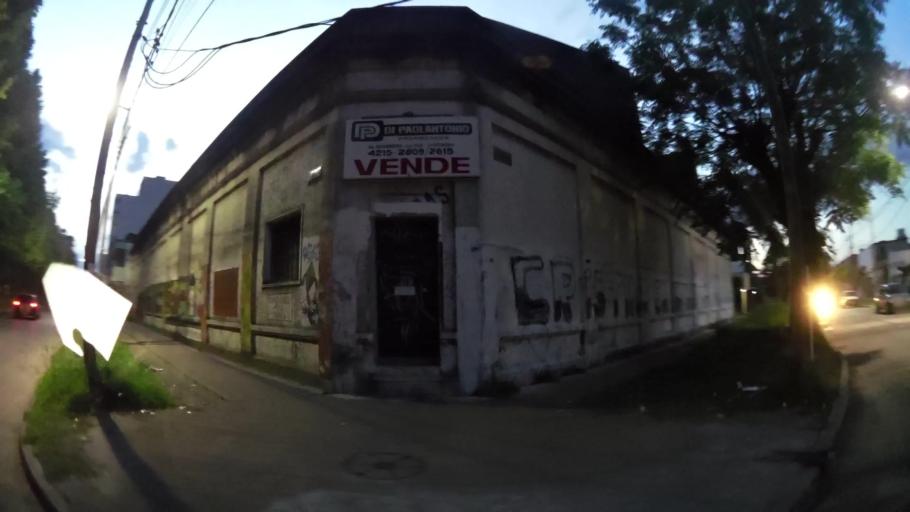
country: AR
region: Buenos Aires
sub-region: Partido de Quilmes
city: Quilmes
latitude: -34.6969
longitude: -58.3092
